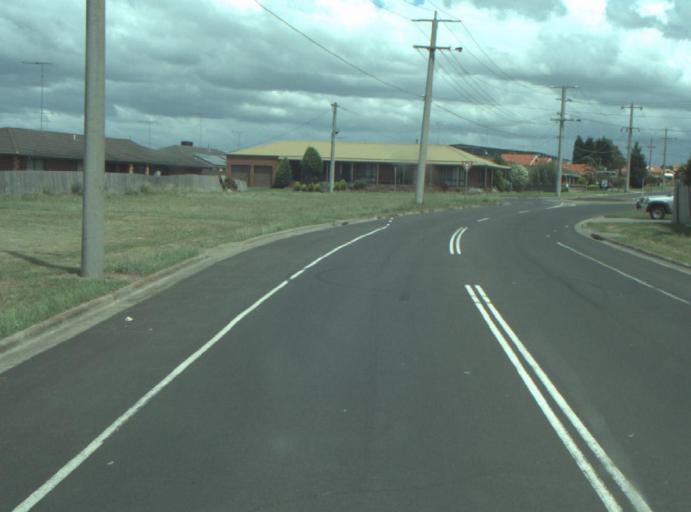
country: AU
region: Victoria
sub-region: Greater Geelong
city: Bell Park
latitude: -38.0927
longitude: 144.3414
